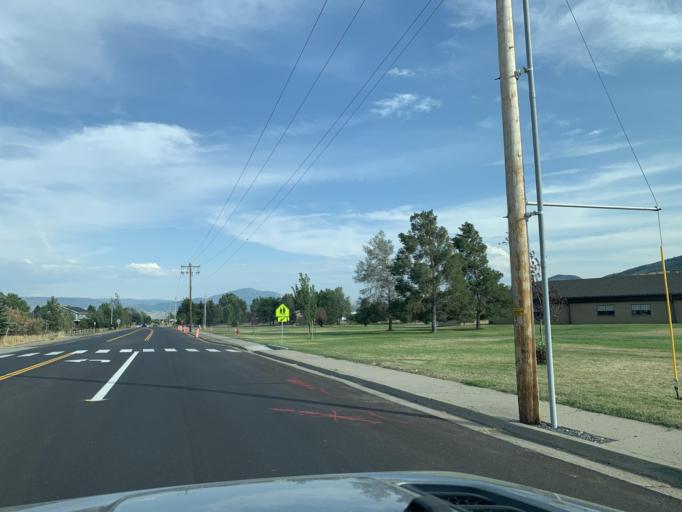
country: US
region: Utah
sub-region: Weber County
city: Wolf Creek
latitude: 41.3084
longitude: -111.8316
